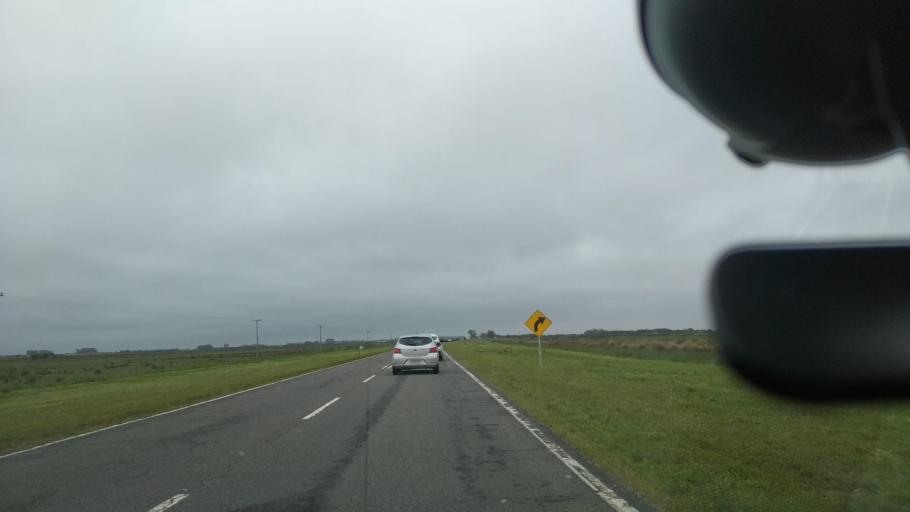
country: AR
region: Buenos Aires
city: Veronica
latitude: -35.6047
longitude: -57.2795
